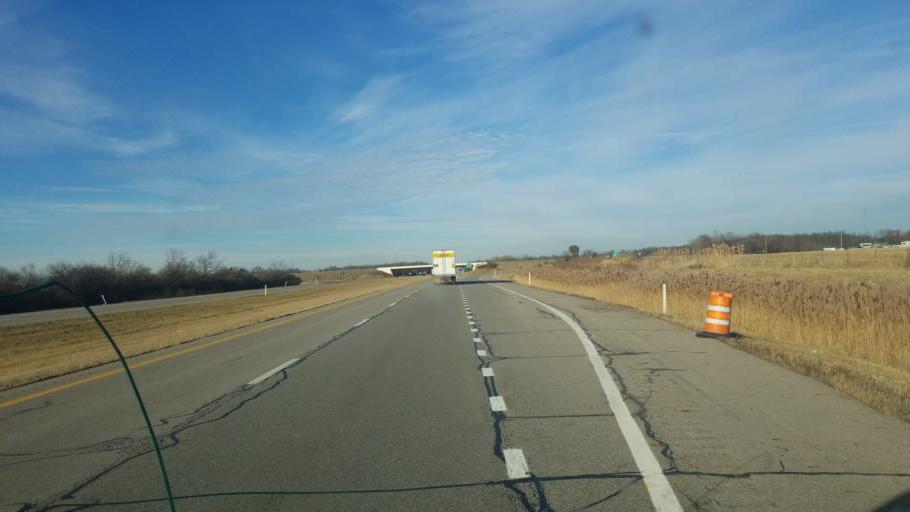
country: US
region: Ohio
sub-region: Ashtabula County
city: Orwell
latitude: 41.5312
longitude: -80.7132
